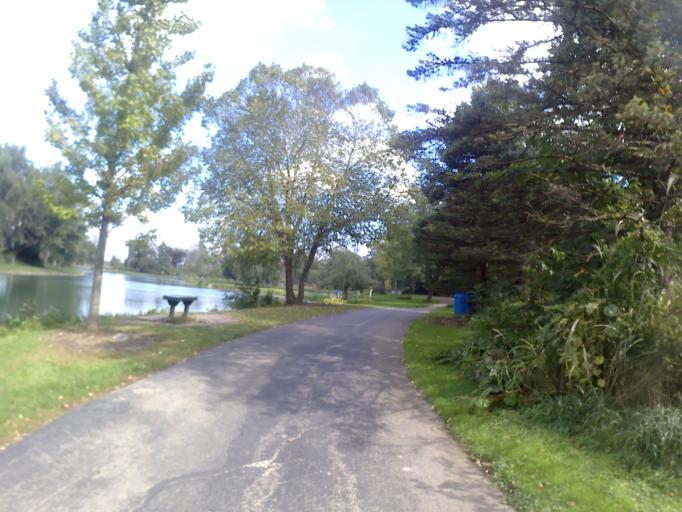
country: US
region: Illinois
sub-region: Will County
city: Bolingbrook
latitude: 41.7107
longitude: -88.0901
